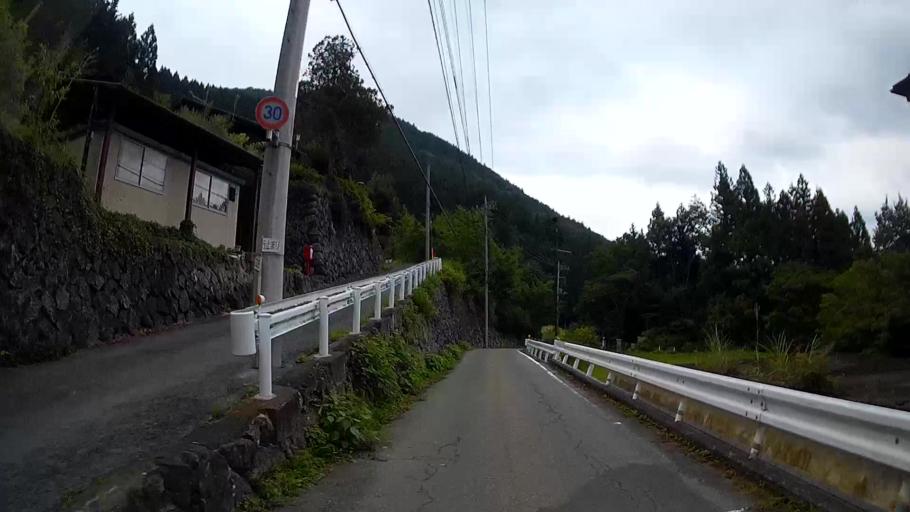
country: JP
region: Saitama
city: Chichibu
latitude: 35.9449
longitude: 138.8844
